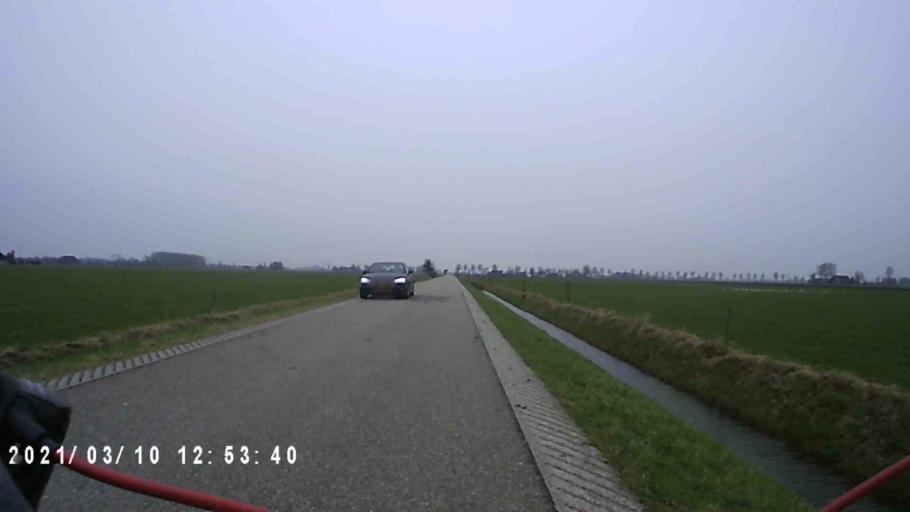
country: NL
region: Groningen
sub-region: Gemeente Bedum
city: Bedum
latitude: 53.2963
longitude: 6.6292
